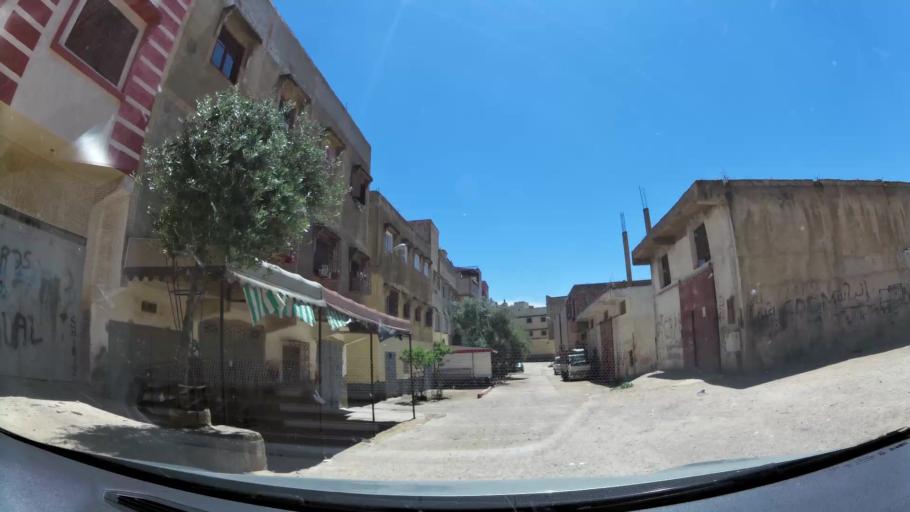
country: MA
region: Meknes-Tafilalet
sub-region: Meknes
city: Meknes
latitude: 33.9054
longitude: -5.5788
